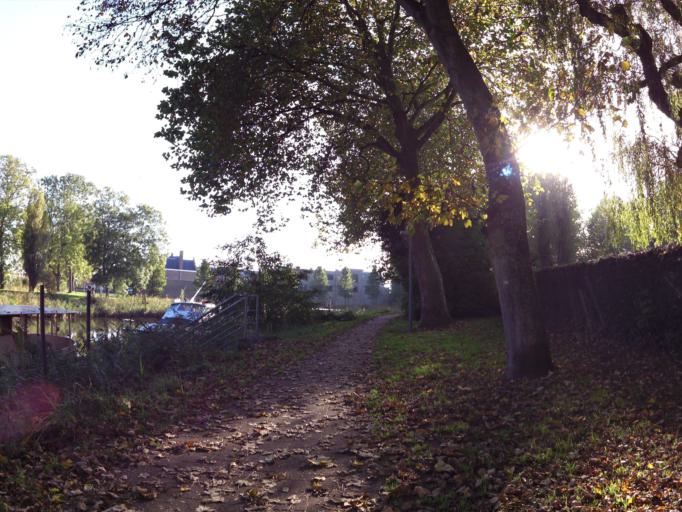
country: BE
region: Flanders
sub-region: Provincie West-Vlaanderen
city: Veurne
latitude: 51.0693
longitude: 2.6670
